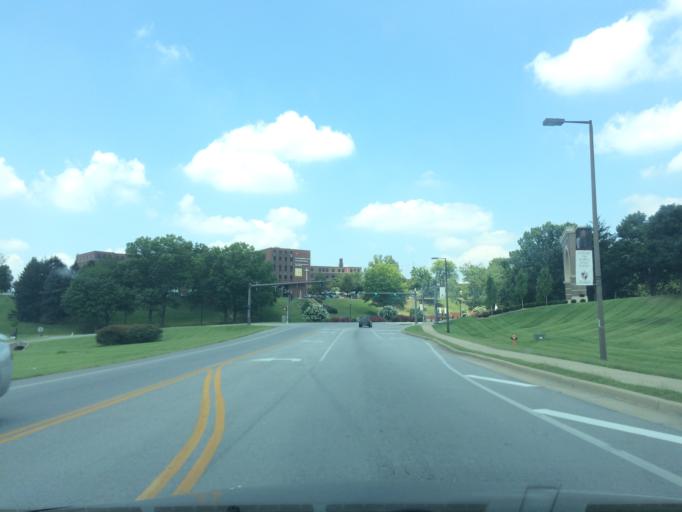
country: US
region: Kentucky
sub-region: Jefferson County
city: Audubon Park
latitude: 38.2165
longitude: -85.7067
